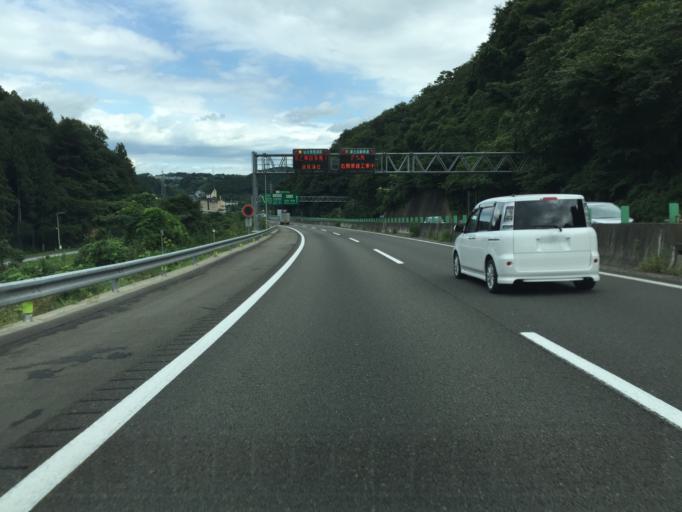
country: JP
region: Miyagi
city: Sendai
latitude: 38.2075
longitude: 140.8040
